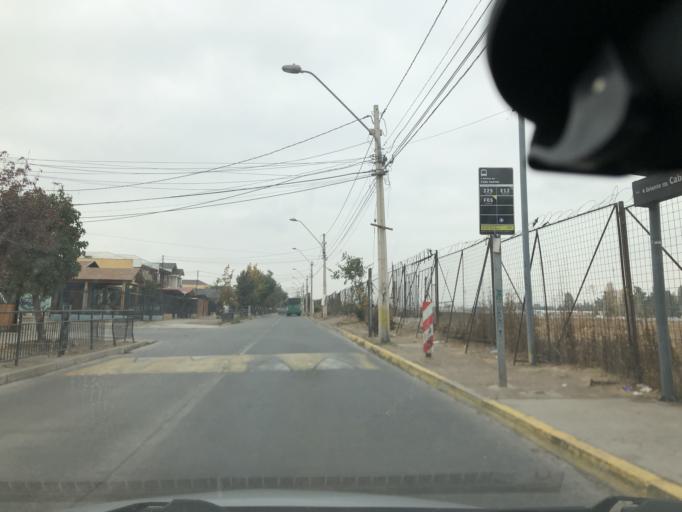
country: CL
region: Santiago Metropolitan
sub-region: Provincia de Santiago
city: La Pintana
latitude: -33.5758
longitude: -70.6103
